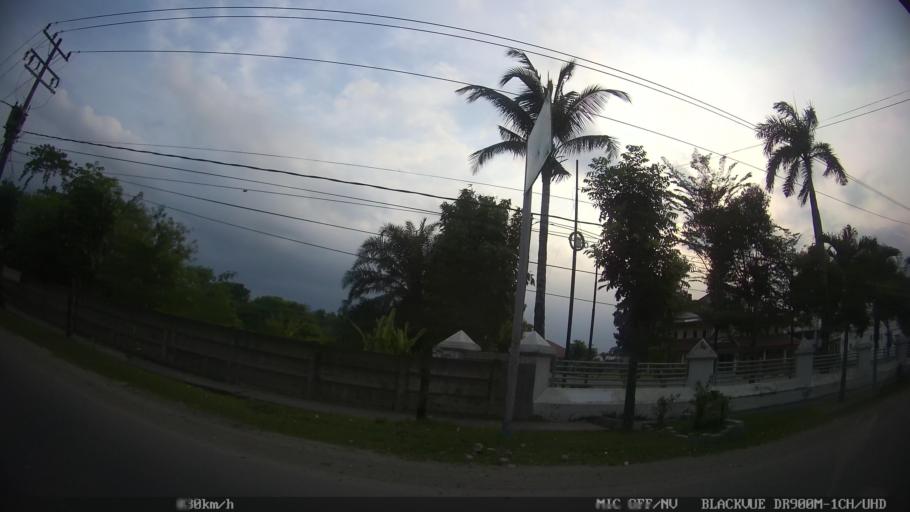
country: ID
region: North Sumatra
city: Sunggal
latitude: 3.5830
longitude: 98.6152
